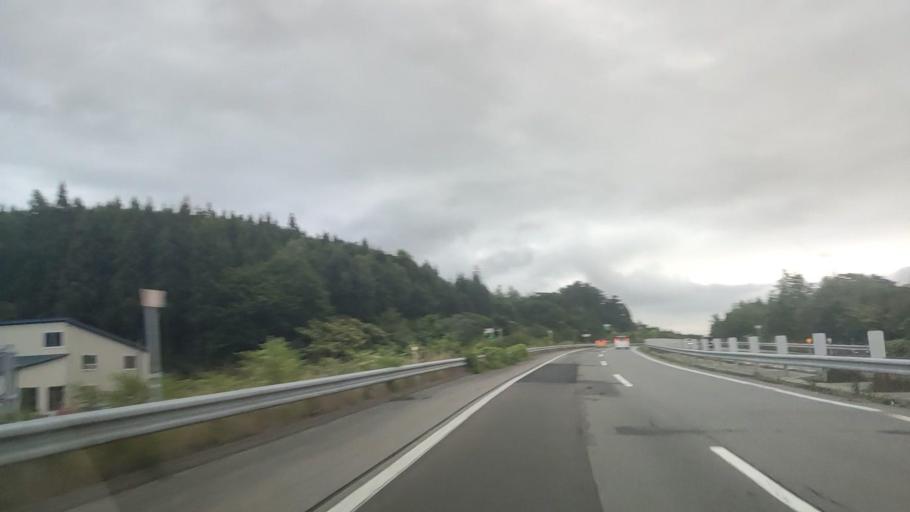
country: JP
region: Hokkaido
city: Nanae
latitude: 41.8987
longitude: 140.7063
